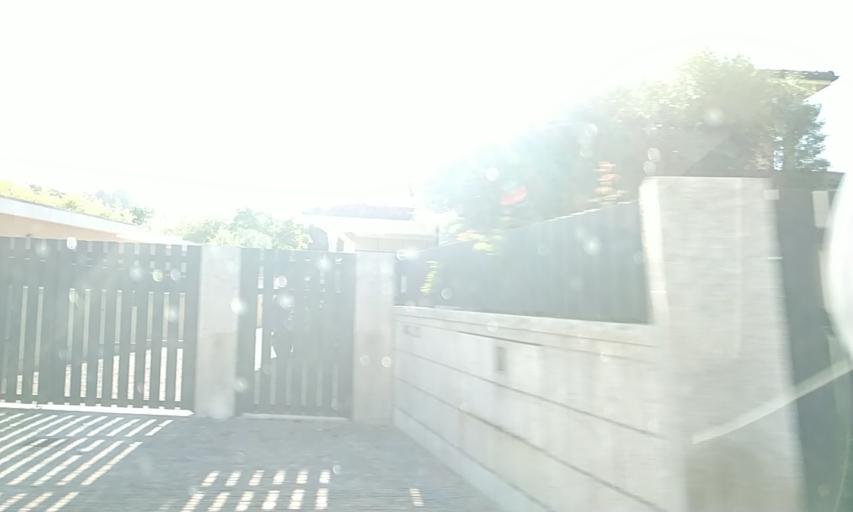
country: PT
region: Porto
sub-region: Santo Tirso
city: Sao Miguel do Couto
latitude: 41.2877
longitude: -8.4717
